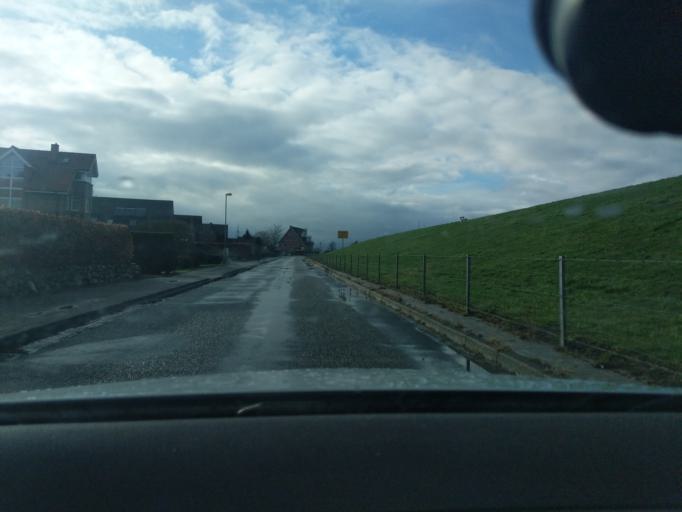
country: DE
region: Schleswig-Holstein
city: Haseldorf
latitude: 53.5922
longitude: 9.5738
